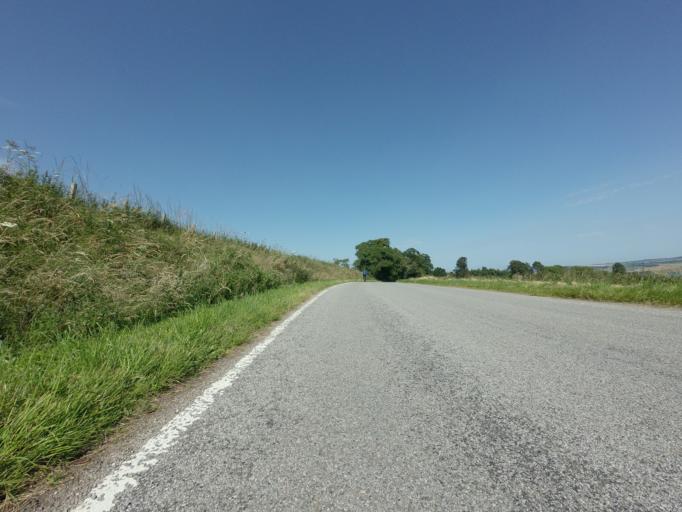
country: GB
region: Scotland
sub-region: Highland
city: Dingwall
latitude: 57.6196
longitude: -4.4022
